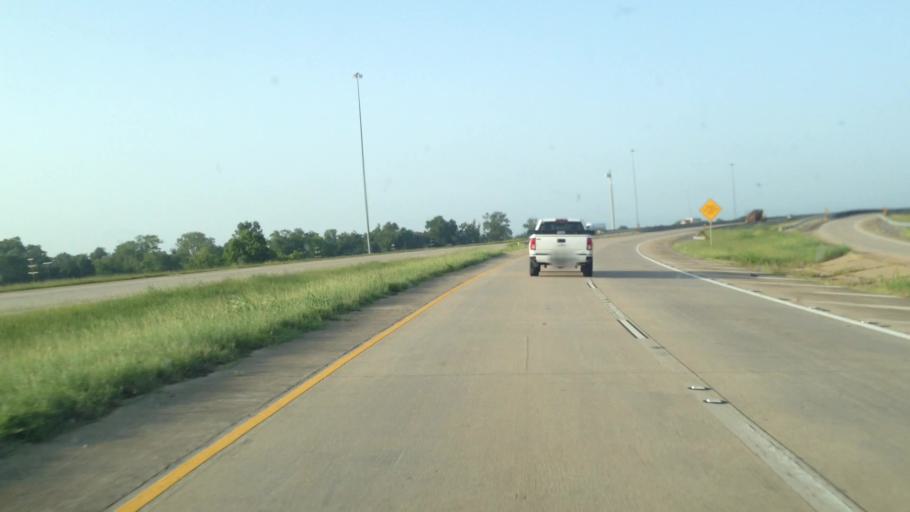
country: US
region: Louisiana
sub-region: Rapides Parish
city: Alexandria
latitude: 31.2465
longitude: -92.4289
